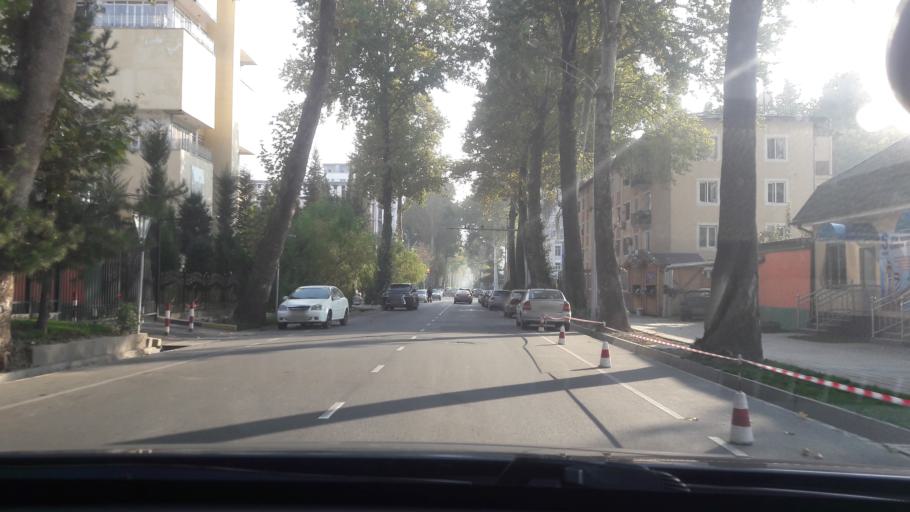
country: TJ
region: Dushanbe
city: Dushanbe
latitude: 38.5799
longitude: 68.7894
